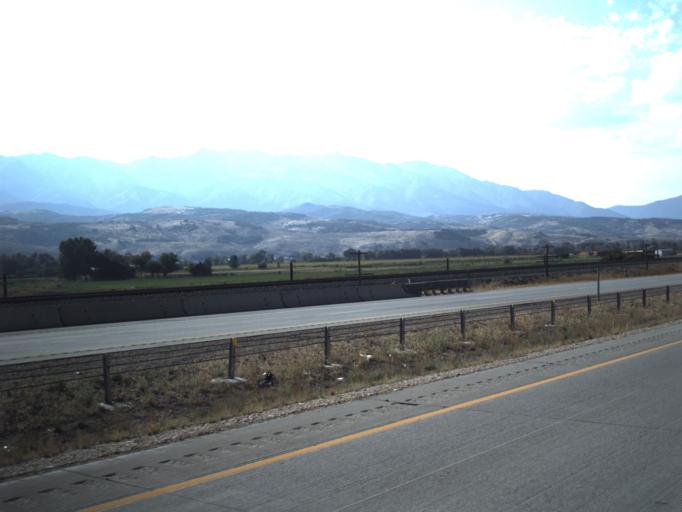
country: US
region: Utah
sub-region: Morgan County
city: Morgan
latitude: 41.0677
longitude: -111.7126
